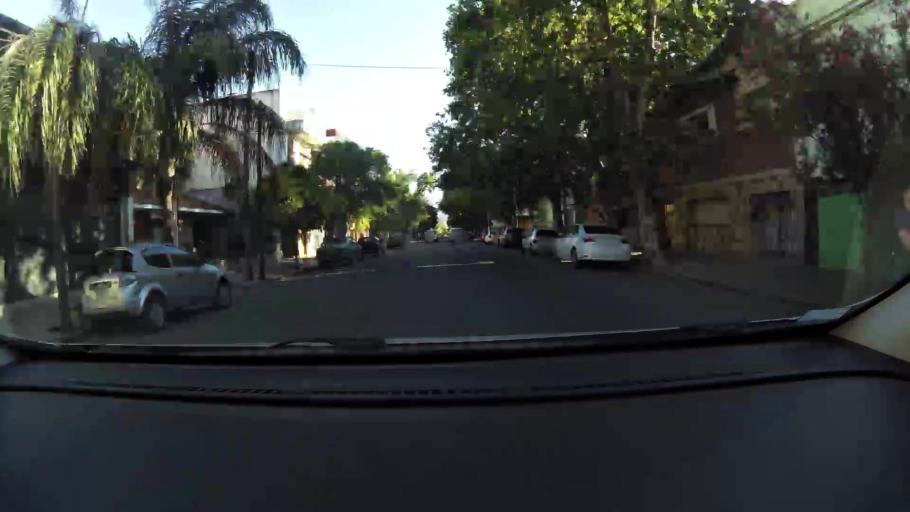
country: AR
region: Cordoba
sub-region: Departamento de Capital
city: Cordoba
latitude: -31.3868
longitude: -64.1838
